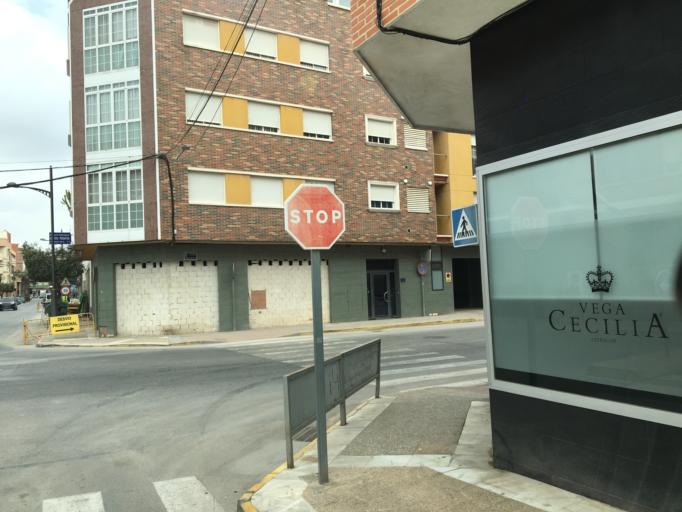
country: ES
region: Murcia
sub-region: Murcia
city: Beniel
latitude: 38.0443
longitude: -1.0005
